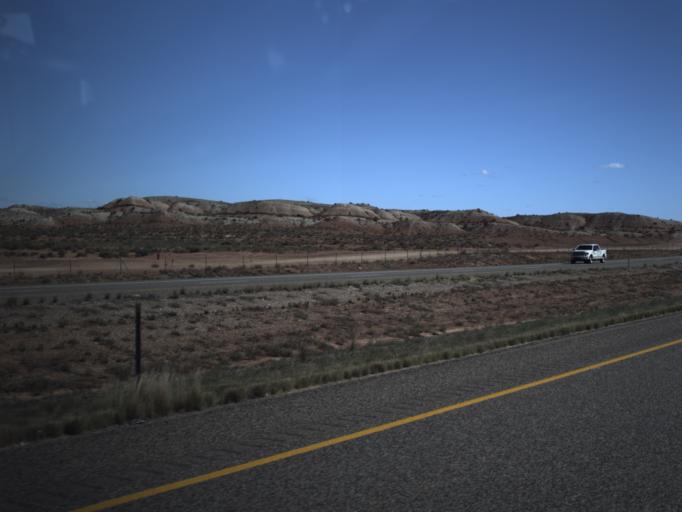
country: US
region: Utah
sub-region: Washington County
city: Saint George
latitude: 37.0008
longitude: -113.5736
